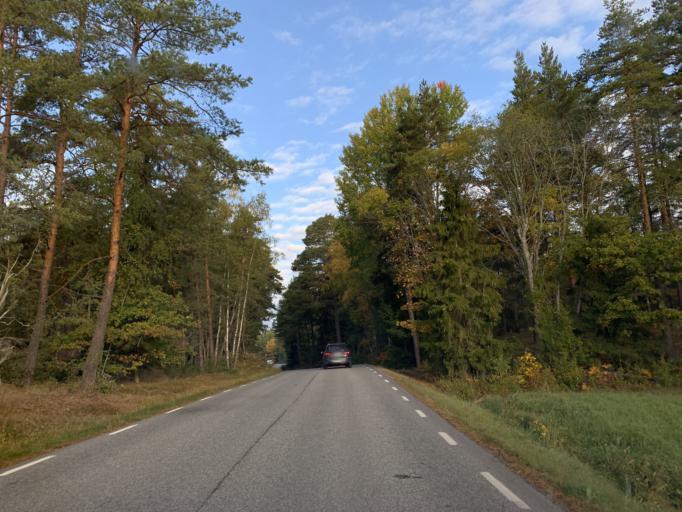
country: SE
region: Stockholm
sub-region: Upplands-Bro Kommun
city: Bro
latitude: 59.5055
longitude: 17.6067
